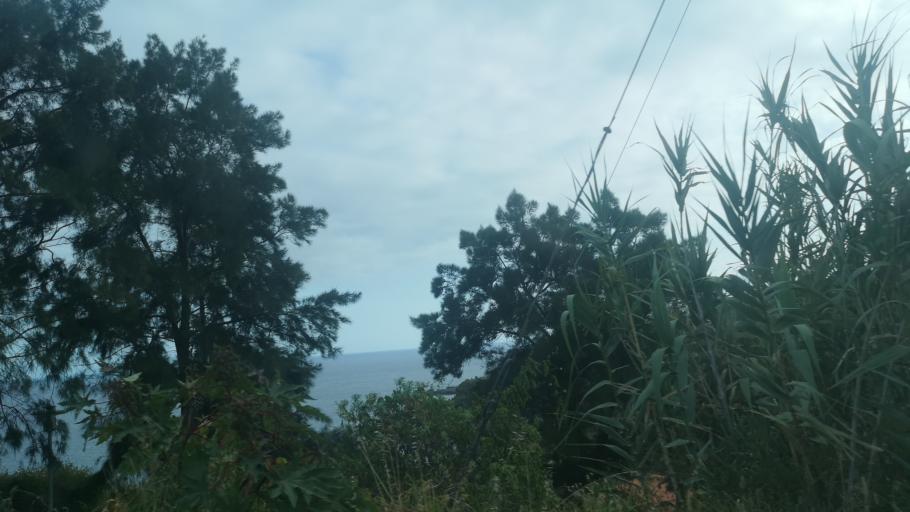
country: PT
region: Madeira
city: Canico
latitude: 32.6524
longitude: -16.8196
